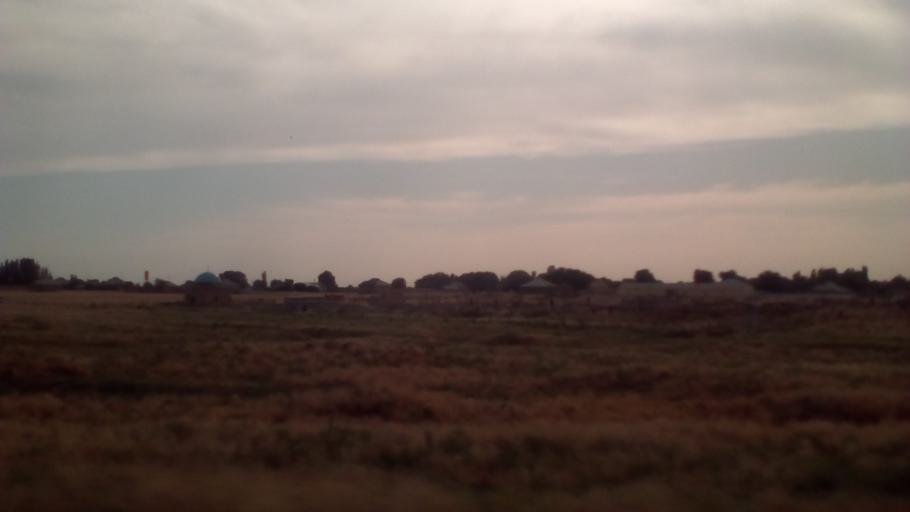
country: KZ
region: Ongtustik Qazaqstan
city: Temirlanovka
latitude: 42.7903
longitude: 69.2051
